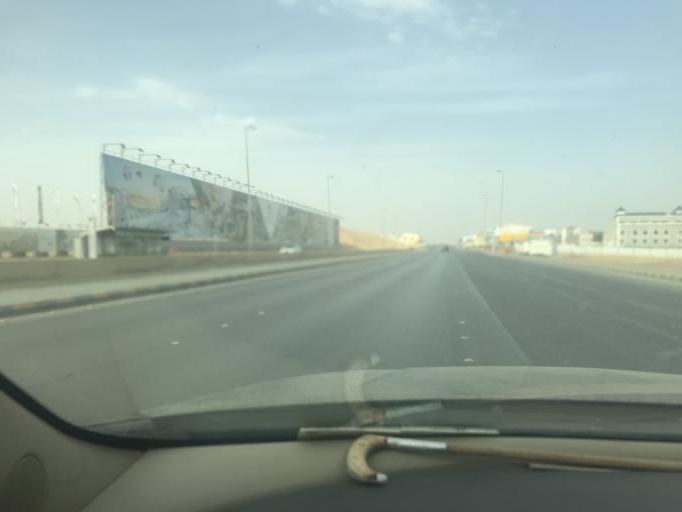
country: SA
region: Ar Riyad
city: Riyadh
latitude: 24.8137
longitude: 46.6778
